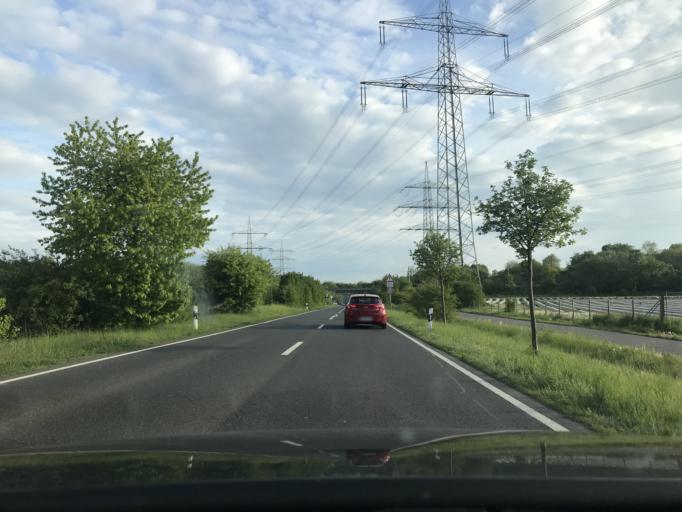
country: DE
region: North Rhine-Westphalia
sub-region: Regierungsbezirk Koln
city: Alfter
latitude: 50.7387
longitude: 7.0340
